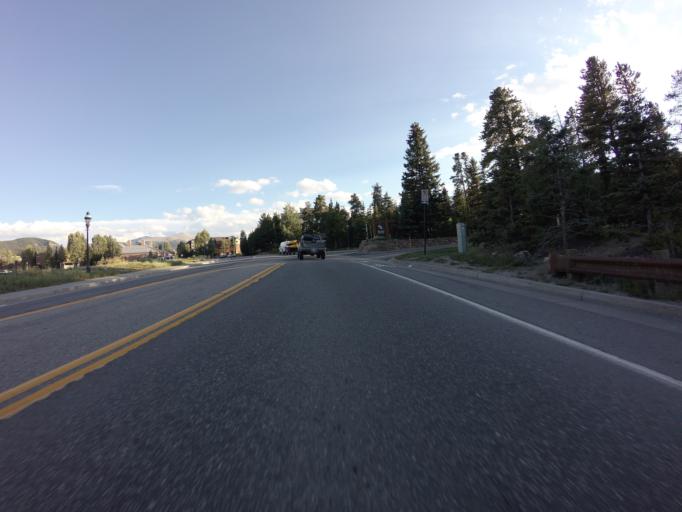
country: US
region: Colorado
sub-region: Summit County
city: Breckenridge
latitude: 39.4838
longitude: -106.0491
